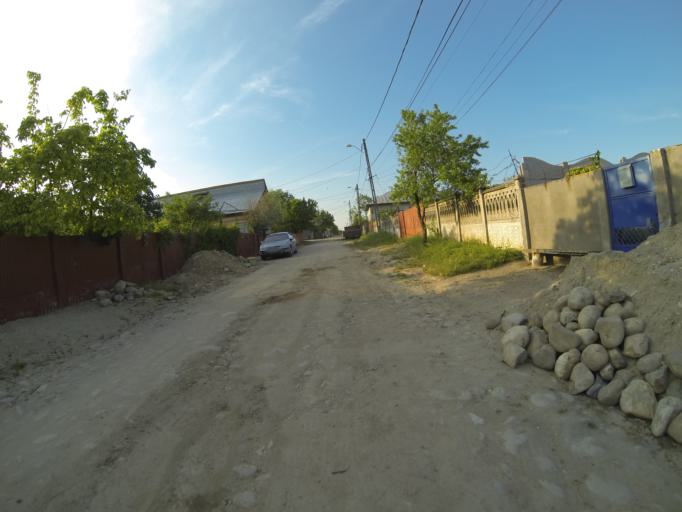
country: RO
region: Dolj
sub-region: Comuna Segarcea
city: Segarcea
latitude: 44.0943
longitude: 23.7469
